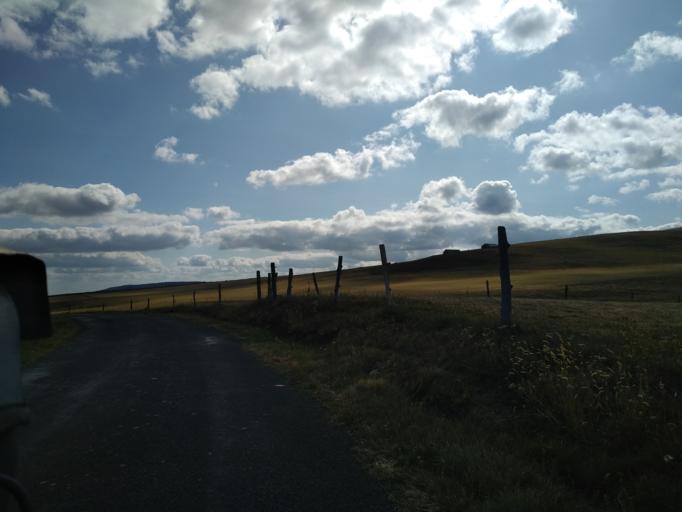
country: FR
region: Auvergne
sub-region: Departement du Cantal
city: Murat
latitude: 45.0251
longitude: 2.8201
